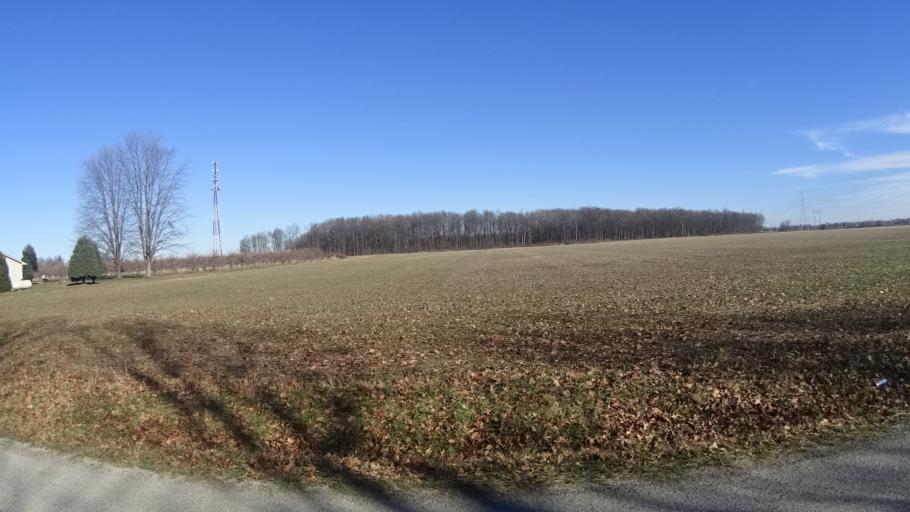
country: US
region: Ohio
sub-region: Lorain County
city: South Amherst
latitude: 41.3611
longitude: -82.2976
